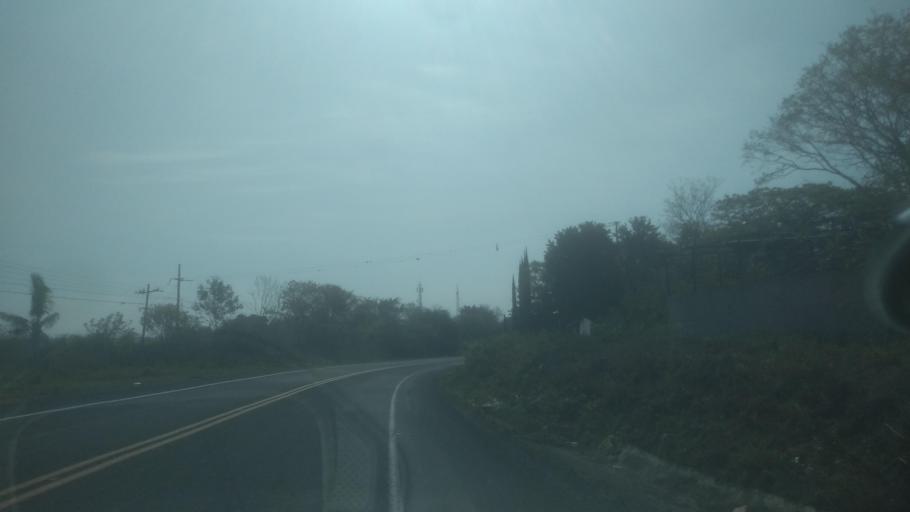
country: MX
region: Veracruz
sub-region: Emiliano Zapata
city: Plan del Rio
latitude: 19.3933
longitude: -96.6251
